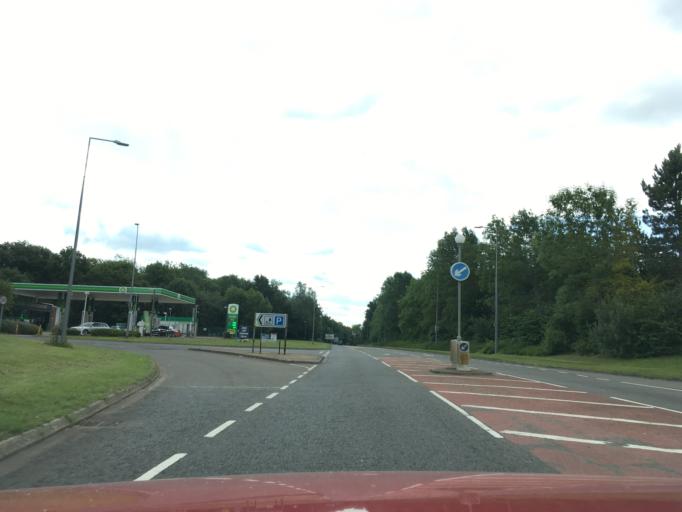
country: GB
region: England
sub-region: Milton Keynes
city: Bradwell
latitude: 52.0534
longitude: -0.7700
